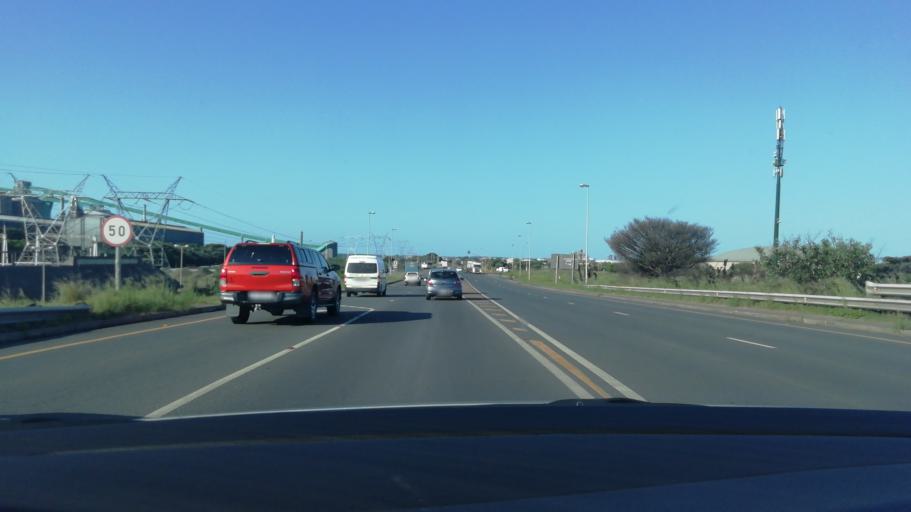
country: ZA
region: KwaZulu-Natal
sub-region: uThungulu District Municipality
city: Richards Bay
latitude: -28.7702
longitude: 32.0345
